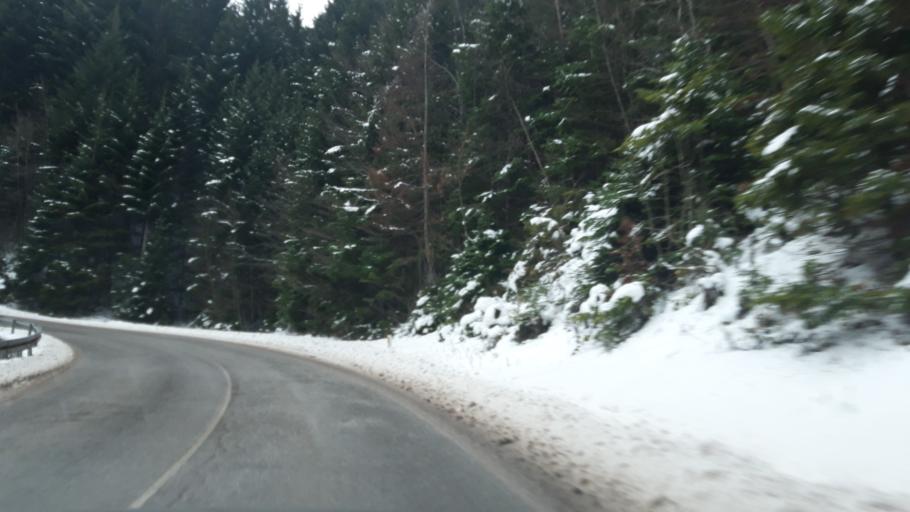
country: BA
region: Republika Srpska
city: Koran
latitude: 43.8018
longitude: 18.5484
